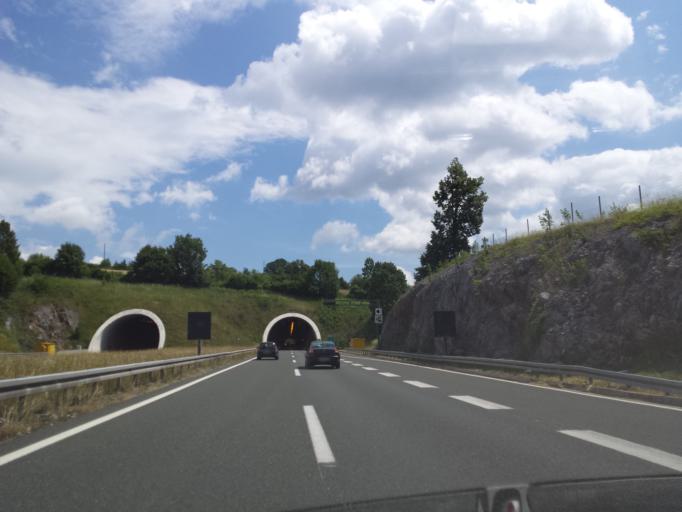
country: HR
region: Primorsko-Goranska
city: Vrbovsko
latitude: 45.3645
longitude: 15.0855
